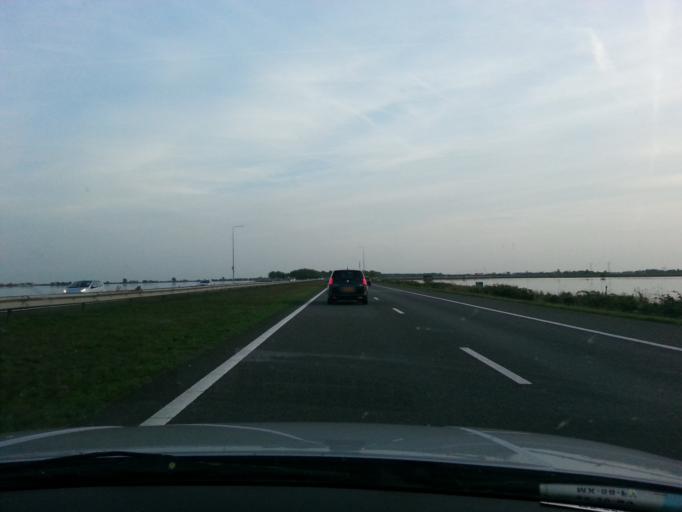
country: NL
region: Friesland
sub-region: Gemeente Skarsterlan
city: Sint Nicolaasga
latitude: 52.9002
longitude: 5.7692
